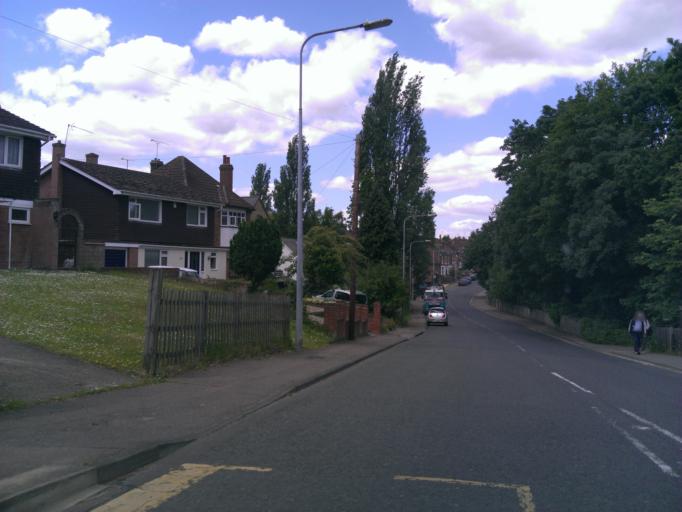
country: GB
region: England
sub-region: Essex
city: Colchester
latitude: 51.8762
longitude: 0.9217
